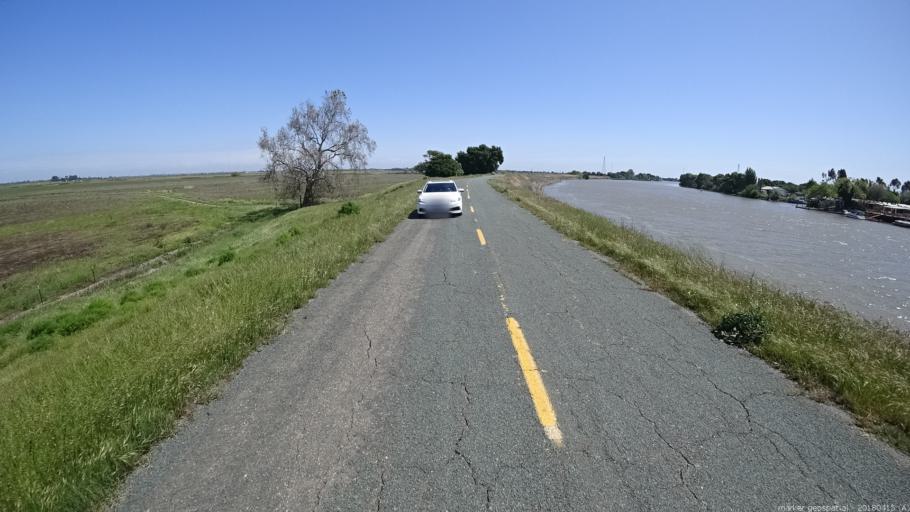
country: US
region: California
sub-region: Solano County
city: Rio Vista
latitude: 38.1735
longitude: -121.6392
